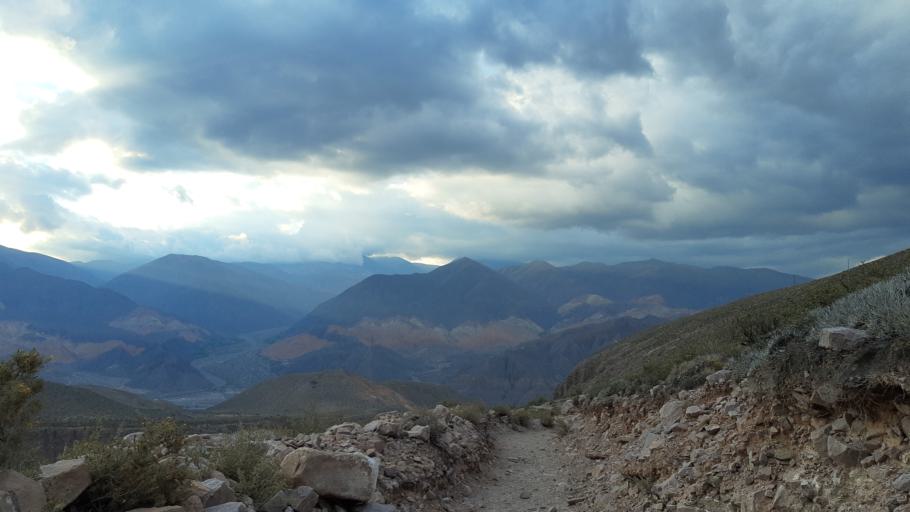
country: AR
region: Jujuy
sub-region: Departamento de Tilcara
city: Tilcara
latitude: -23.5914
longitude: -65.3836
